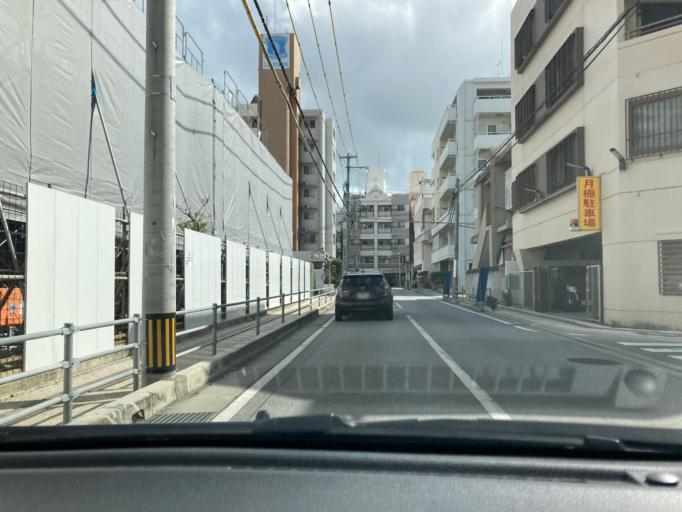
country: JP
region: Okinawa
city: Naha-shi
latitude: 26.2114
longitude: 127.6791
